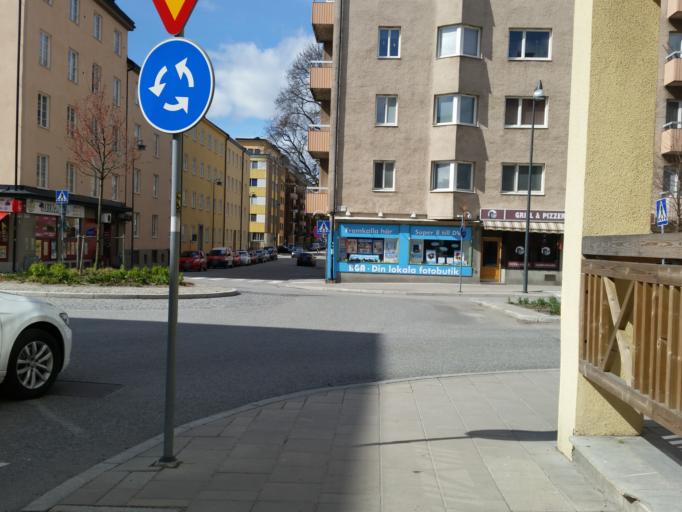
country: SE
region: Stockholm
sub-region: Sundbybergs Kommun
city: Sundbyberg
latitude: 59.3653
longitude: 17.9637
